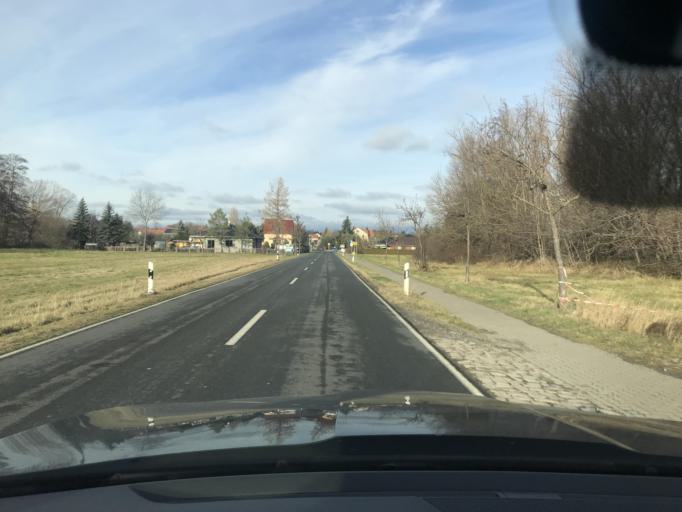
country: DE
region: Saxony-Anhalt
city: Weddersleben
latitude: 51.7586
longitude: 11.0907
